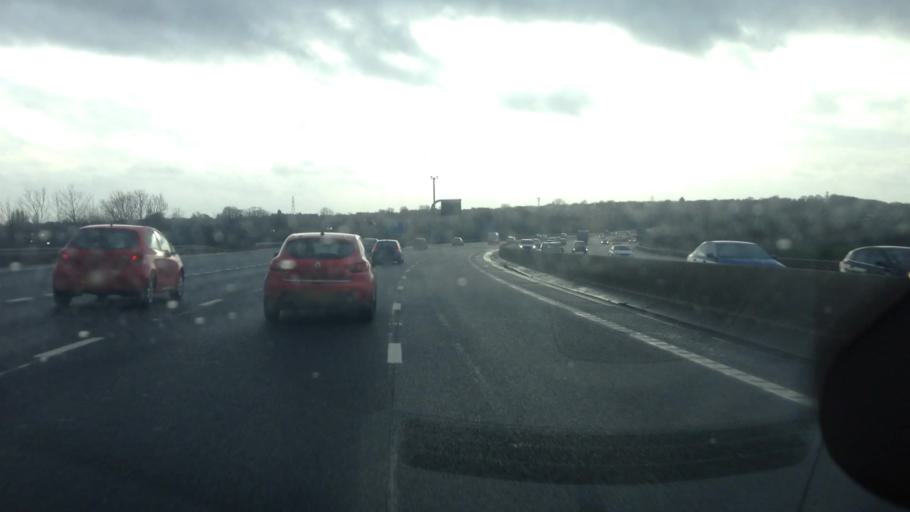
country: GB
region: England
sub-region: City and Borough of Wakefield
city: Crigglestone
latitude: 53.6548
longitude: -1.5281
